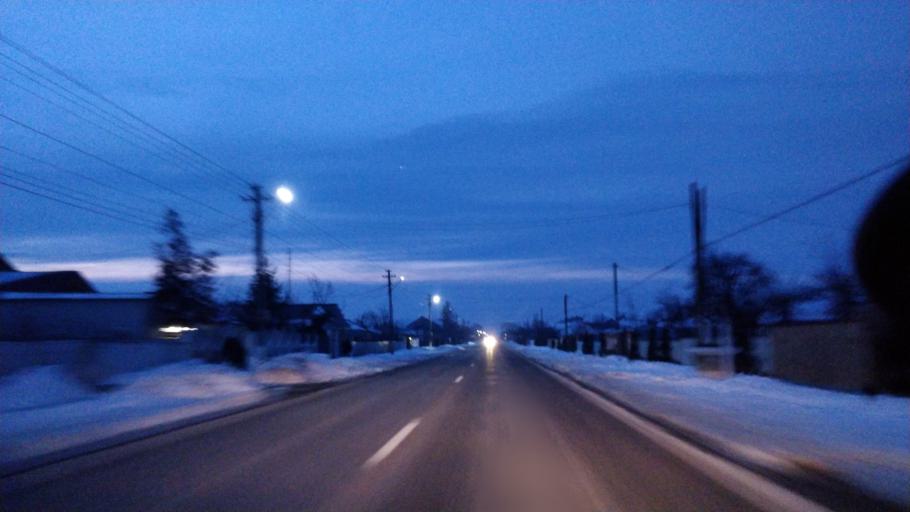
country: RO
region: Vrancea
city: Vulturu de Sus
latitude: 45.6202
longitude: 27.4089
